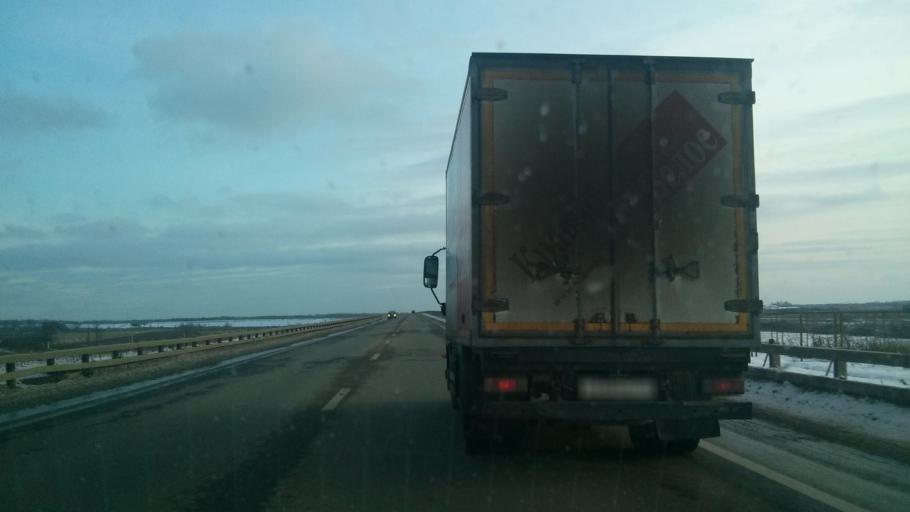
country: RU
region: Vladimir
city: Murom
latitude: 55.5931
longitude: 42.1160
